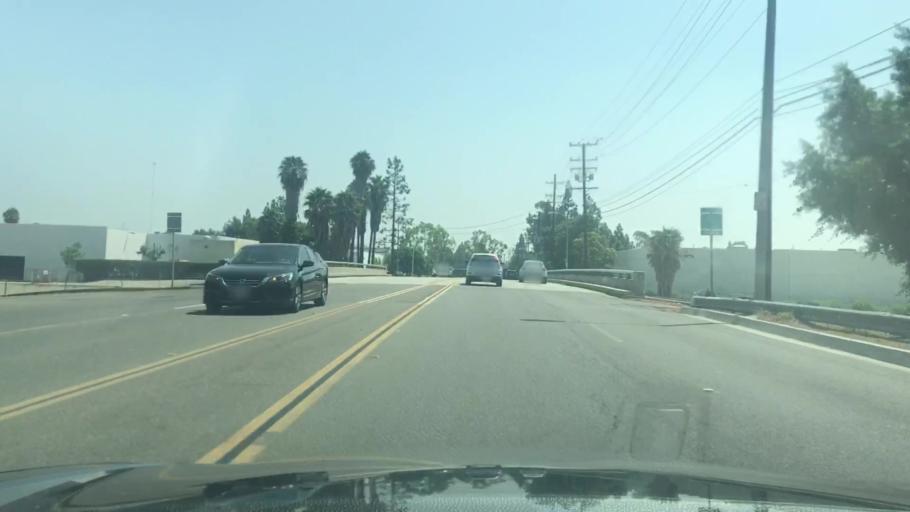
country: US
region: California
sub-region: Orange County
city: La Palma
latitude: 33.8733
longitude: -118.0337
